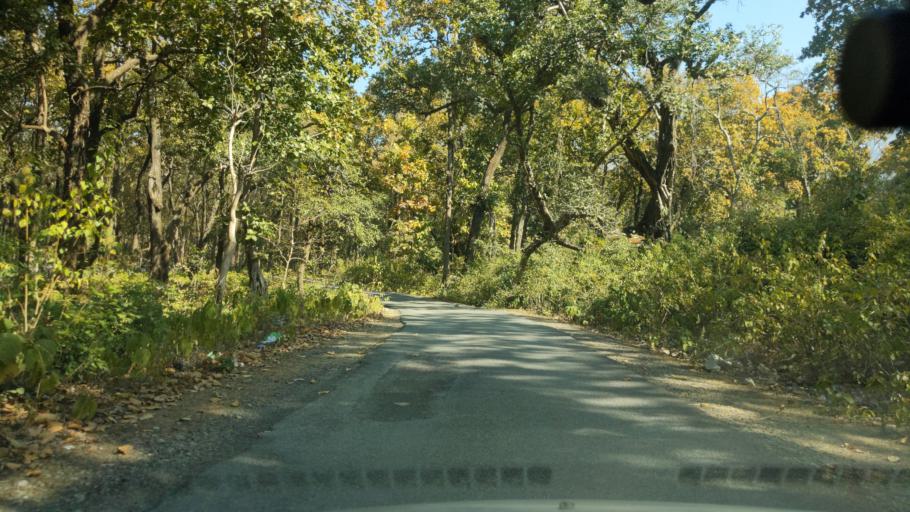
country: IN
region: Uttarakhand
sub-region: Naini Tal
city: Ramnagar
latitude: 29.4648
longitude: 79.2322
